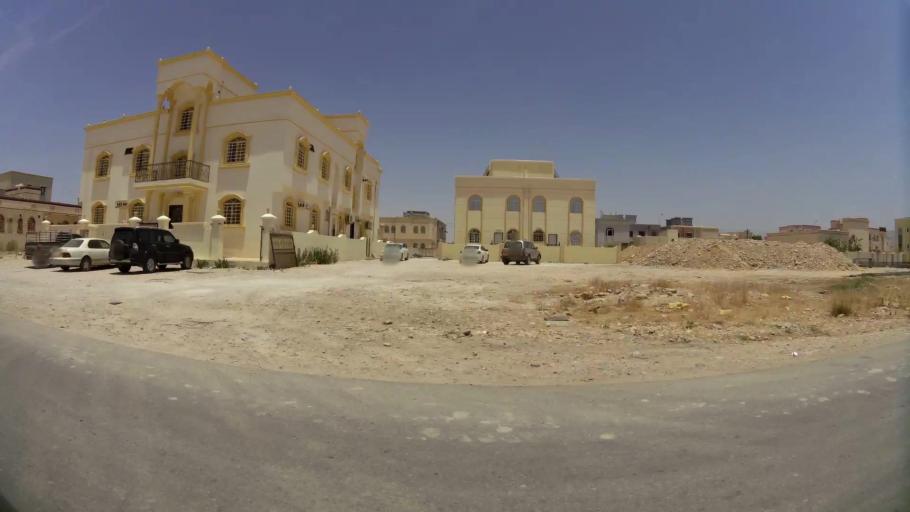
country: OM
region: Zufar
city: Salalah
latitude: 17.0925
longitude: 54.1599
